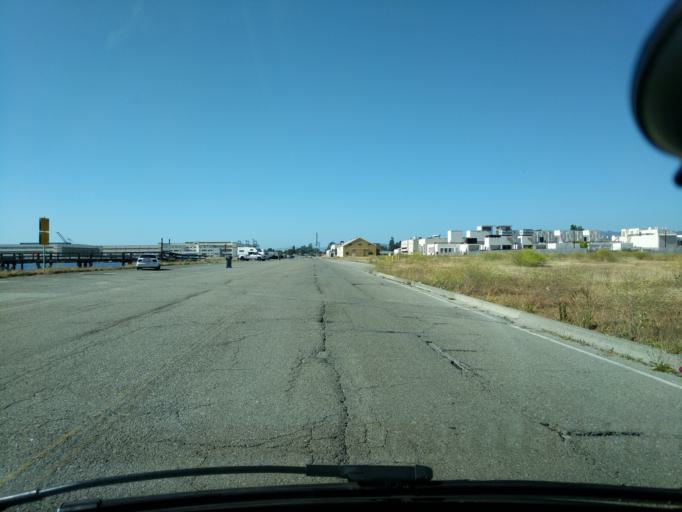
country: US
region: California
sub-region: Alameda County
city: Oakland
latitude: 37.7767
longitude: -122.2983
